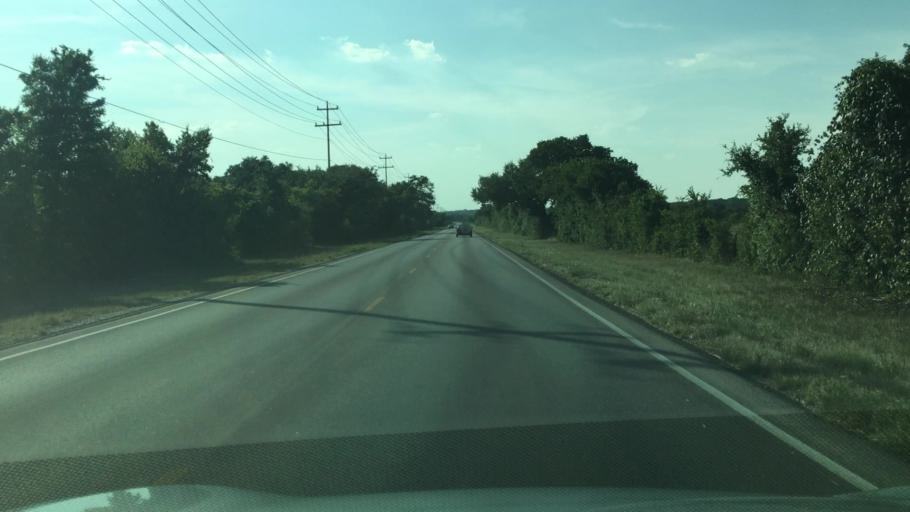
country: US
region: Texas
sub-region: Travis County
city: Shady Hollow
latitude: 30.1067
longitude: -97.9434
